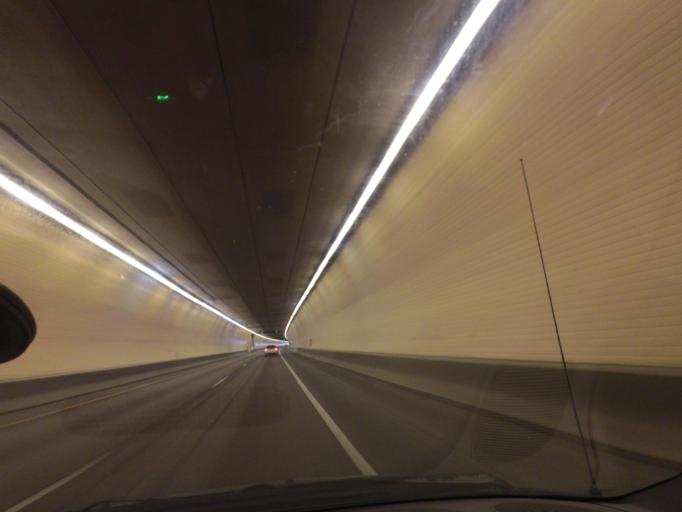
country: US
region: Colorado
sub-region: Garfield County
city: Glenwood Springs
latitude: 39.5862
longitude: -107.1865
